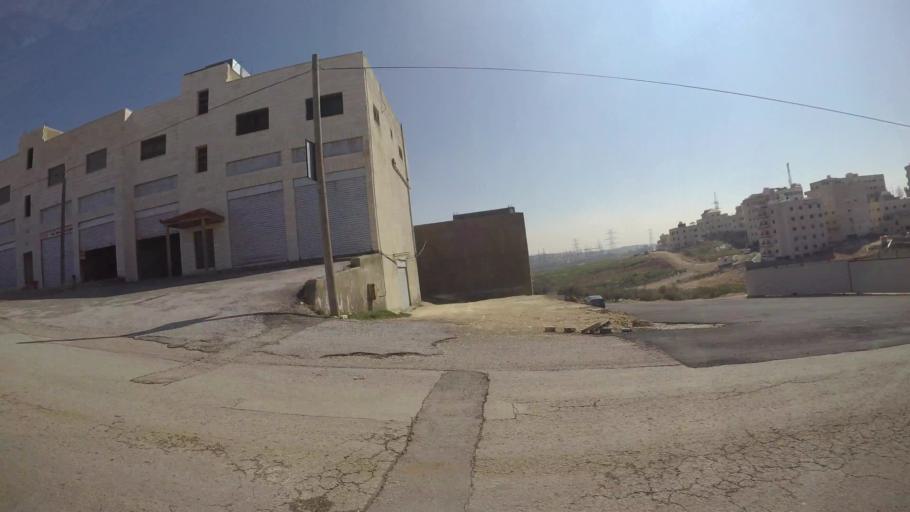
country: JO
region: Amman
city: Al Bunayyat ash Shamaliyah
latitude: 31.8955
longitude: 35.8979
